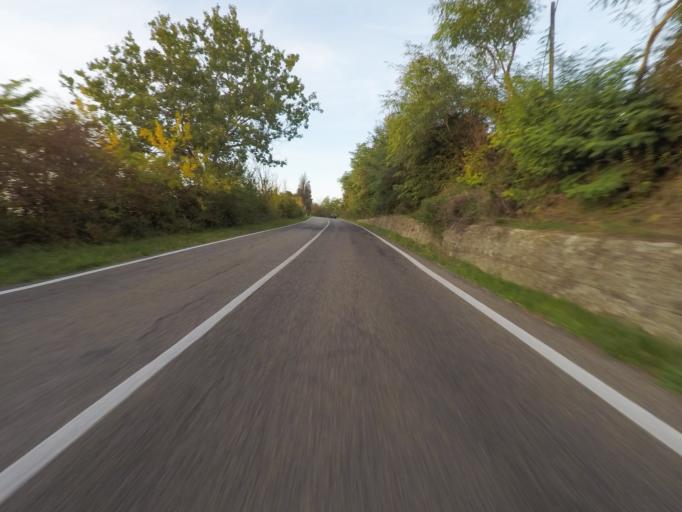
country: IT
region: Tuscany
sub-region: Provincia di Siena
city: Pienza
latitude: 43.1001
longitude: 11.6965
